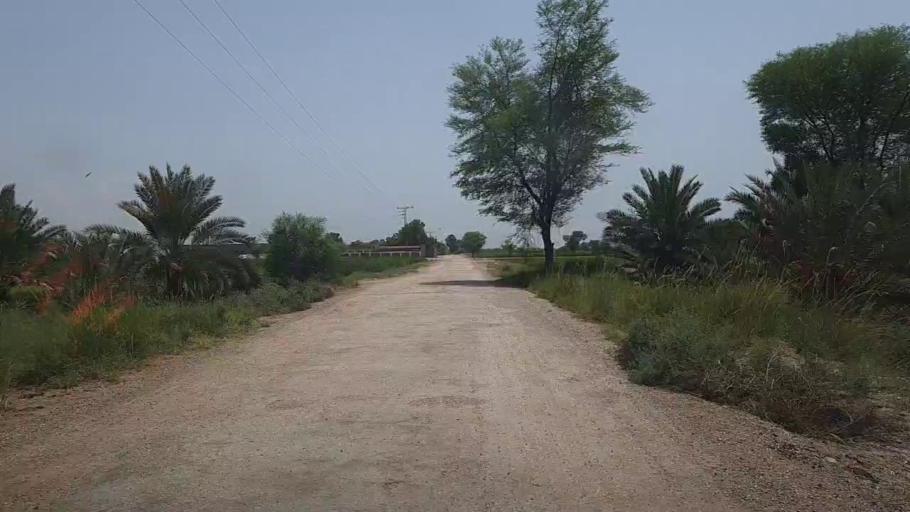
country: PK
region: Sindh
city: Pad Idan
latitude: 26.8462
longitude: 68.3247
